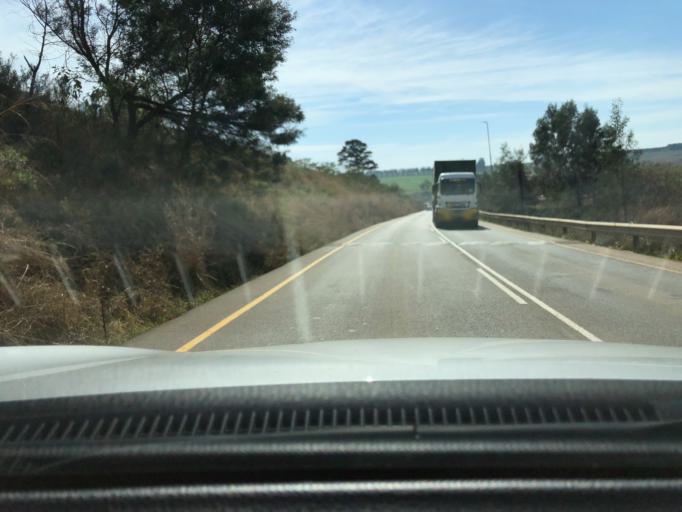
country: ZA
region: KwaZulu-Natal
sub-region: Sisonke District Municipality
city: Ixopo
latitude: -30.1494
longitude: 30.0666
